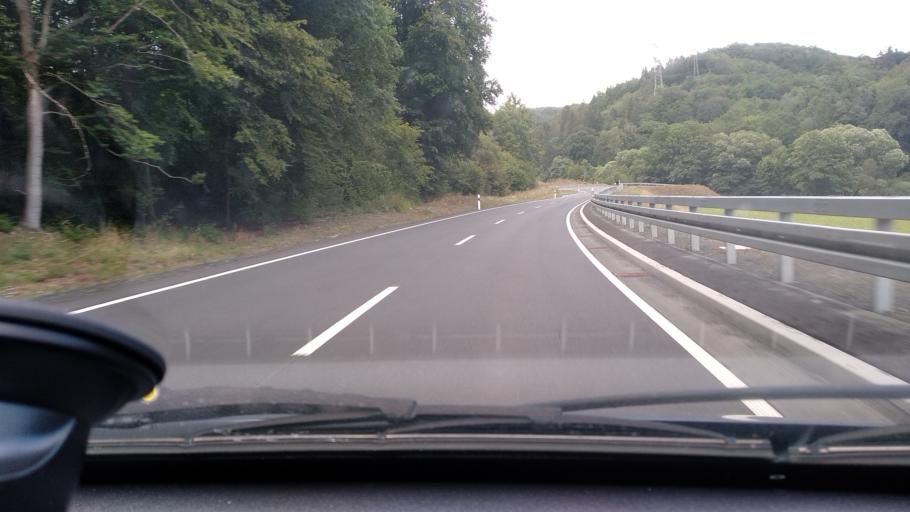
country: DE
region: Hesse
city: Dillenburg
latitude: 50.7460
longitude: 8.3041
